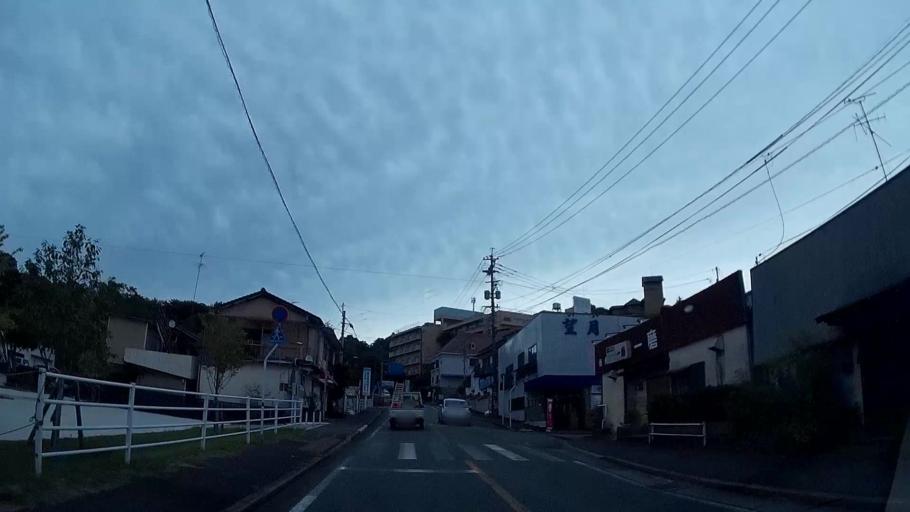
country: JP
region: Kumamoto
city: Kikuchi
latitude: 32.9849
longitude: 130.8149
